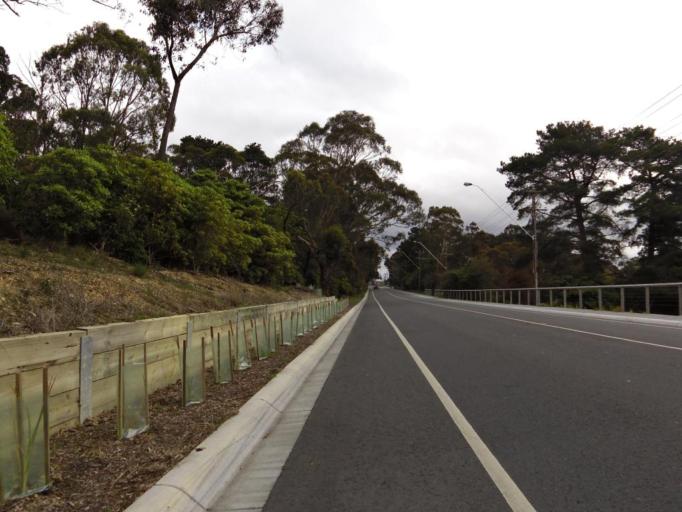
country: AU
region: Victoria
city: Mitcham
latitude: -37.7954
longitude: 145.1971
